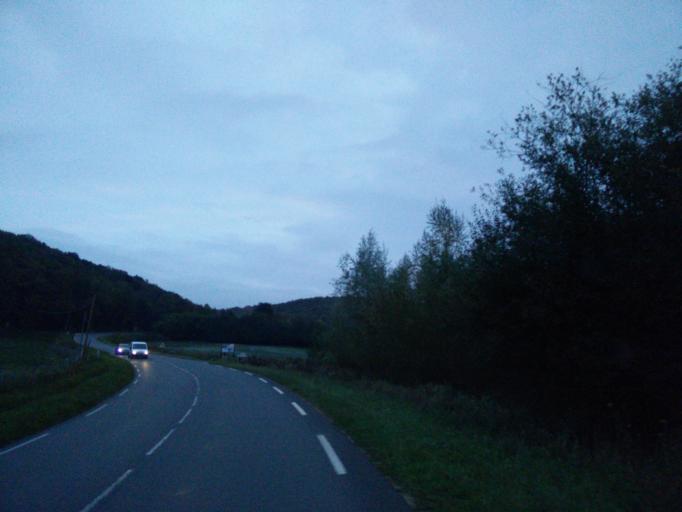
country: FR
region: Aquitaine
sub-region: Departement de la Dordogne
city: Saint-Cyprien
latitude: 44.9064
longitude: 1.1173
